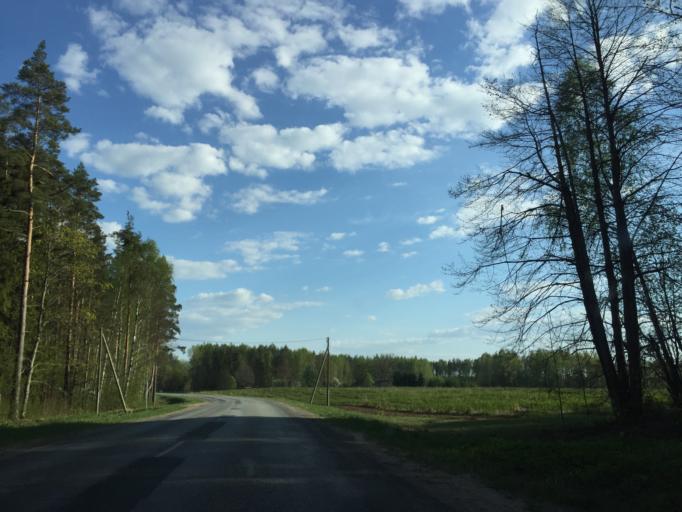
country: LV
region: Sigulda
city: Sigulda
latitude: 57.2192
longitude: 24.8557
